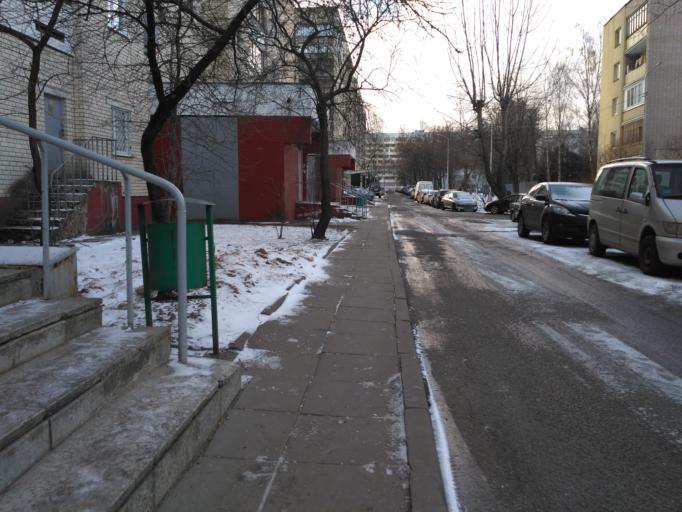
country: BY
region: Minsk
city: Minsk
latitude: 53.9209
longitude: 27.5736
